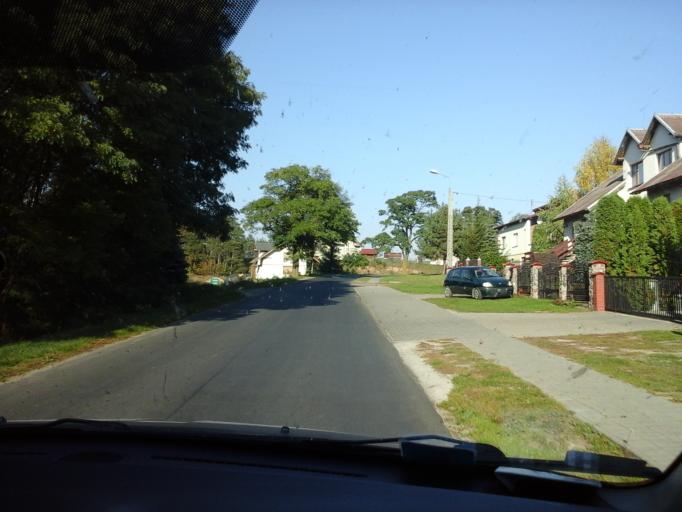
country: PL
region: Kujawsko-Pomorskie
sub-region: Powiat brodnicki
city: Bartniczka
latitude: 53.2507
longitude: 19.6174
